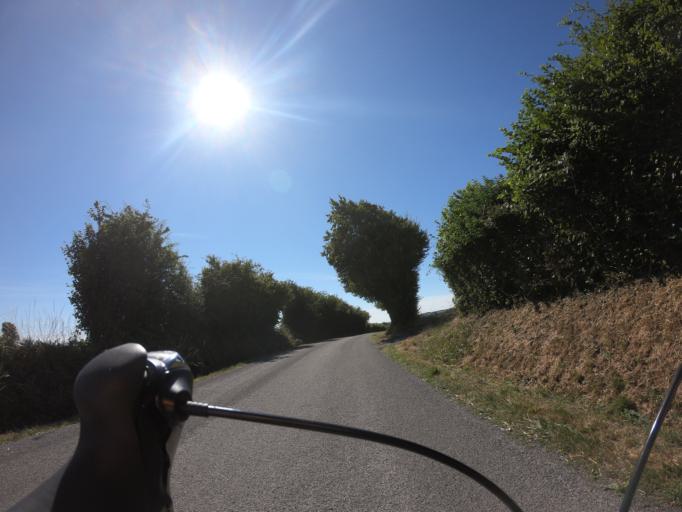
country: FR
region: Lower Normandy
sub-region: Departement de l'Orne
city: Saint-Denis-sur-Sarthon
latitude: 48.5371
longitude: -0.0977
